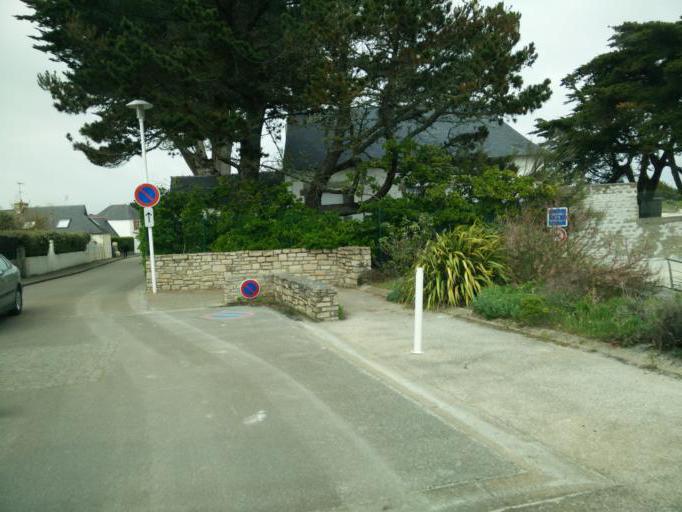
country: FR
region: Brittany
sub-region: Departement du Finistere
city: Loctudy
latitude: 47.8120
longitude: -4.1752
